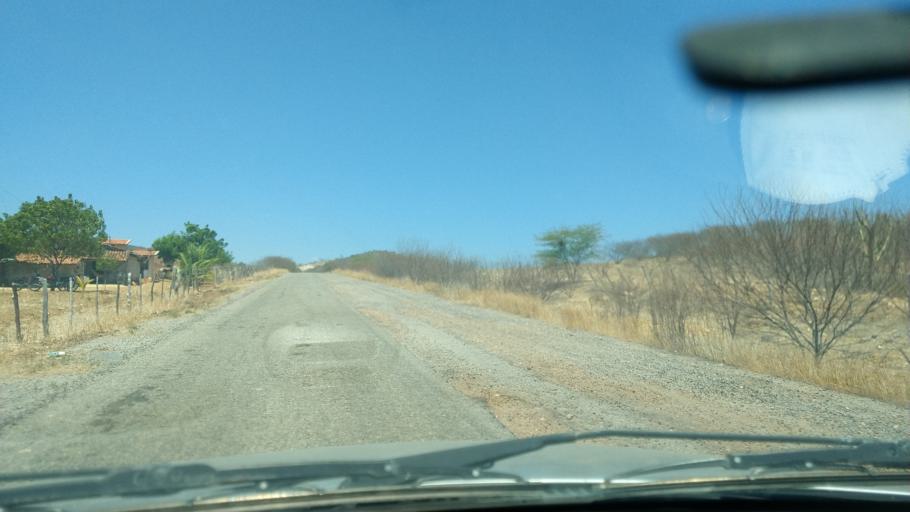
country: BR
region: Rio Grande do Norte
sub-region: Sao Tome
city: Sao Tome
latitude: -5.9746
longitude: -36.1508
